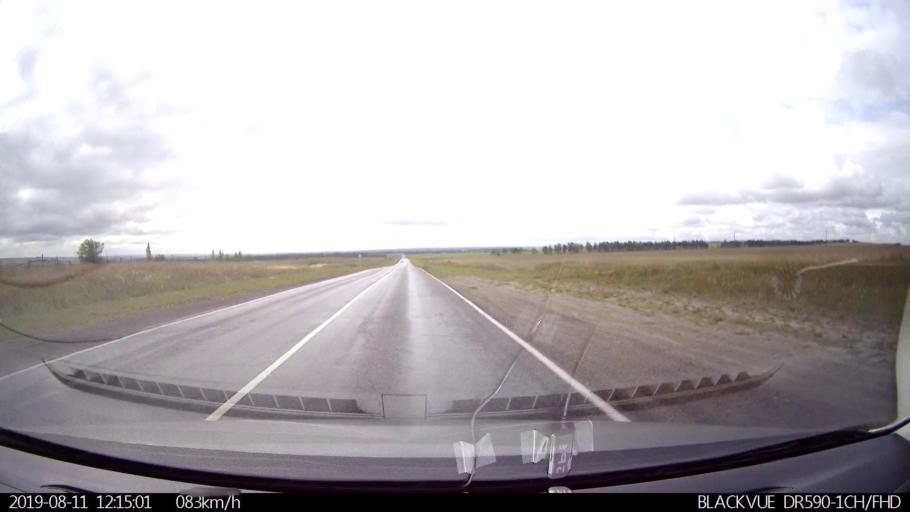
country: RU
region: Ulyanovsk
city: Ignatovka
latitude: 53.9463
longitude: 47.9727
